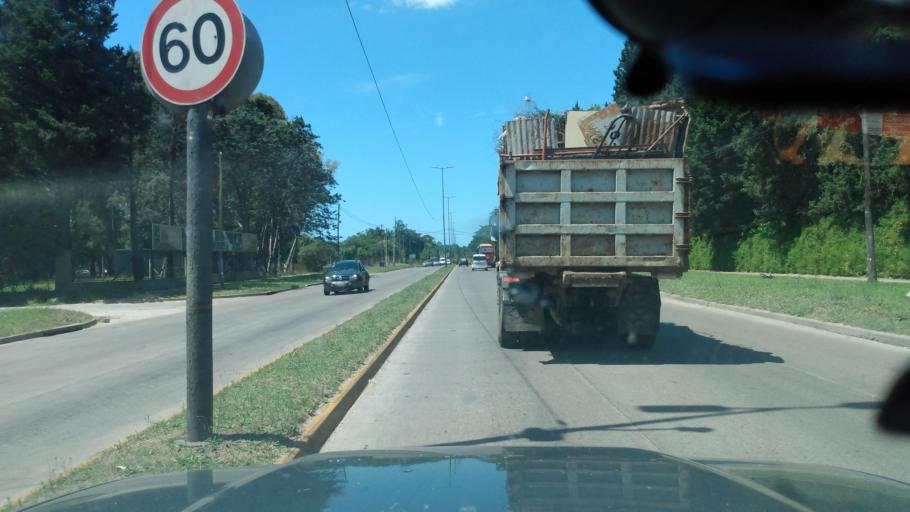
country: AR
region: Buenos Aires
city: Hurlingham
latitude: -34.5600
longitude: -58.7317
